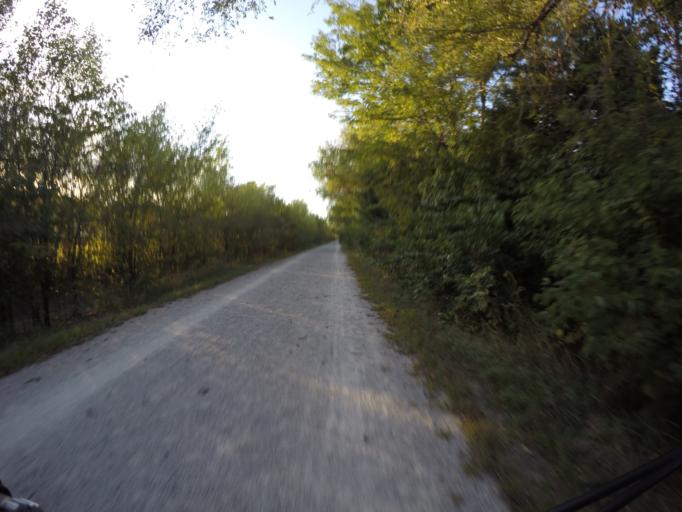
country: US
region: Kansas
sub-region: Riley County
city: Manhattan
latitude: 39.1779
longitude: -96.6034
